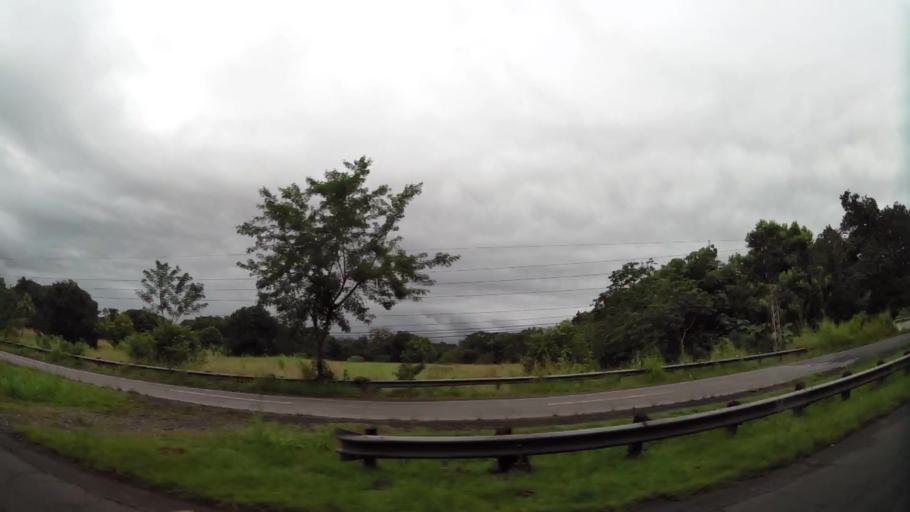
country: PA
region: Chiriqui
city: Tijera
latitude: 8.4723
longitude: -82.5413
